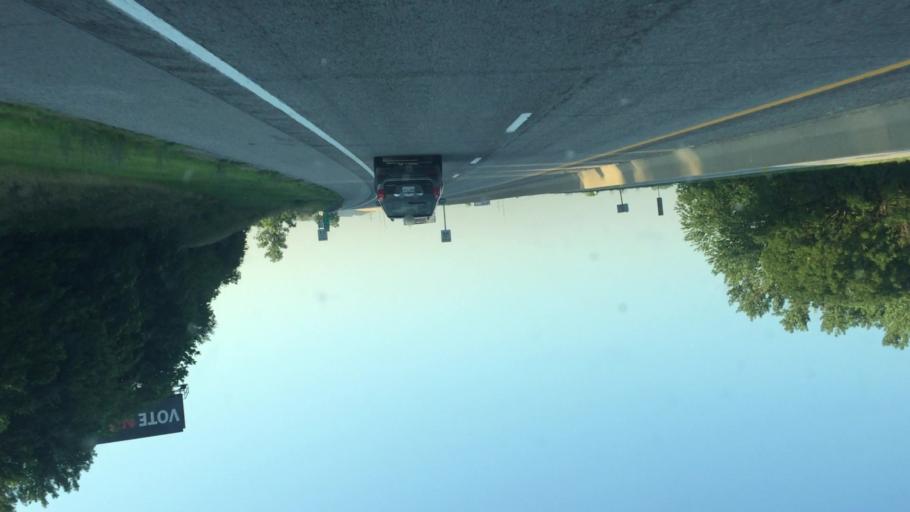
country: US
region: Kansas
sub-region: Doniphan County
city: Elwood
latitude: 39.7360
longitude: -94.8502
